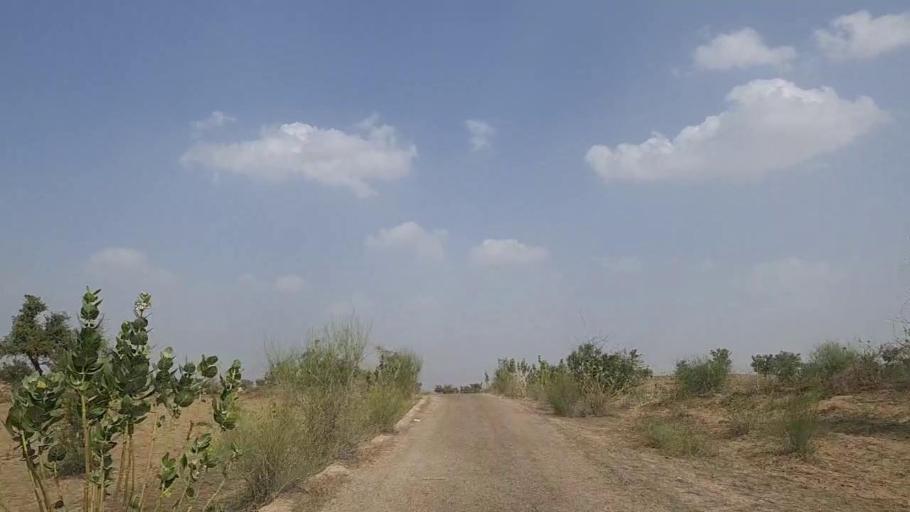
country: PK
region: Sindh
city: Islamkot
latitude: 24.8301
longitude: 70.1506
